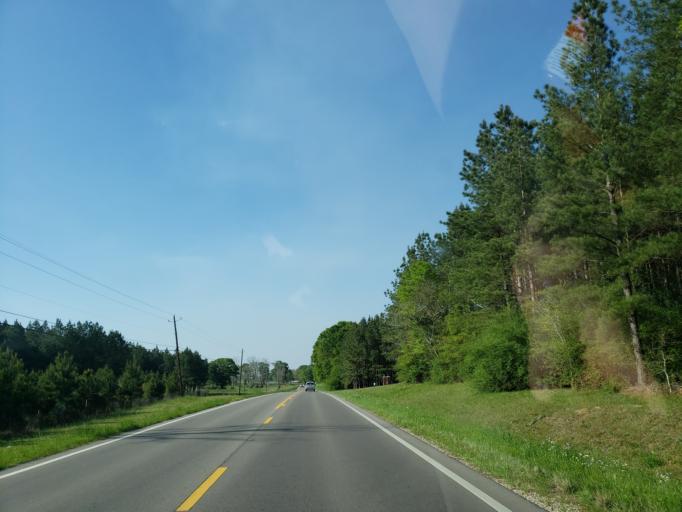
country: US
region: Mississippi
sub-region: Perry County
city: Richton
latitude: 31.3769
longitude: -88.9361
